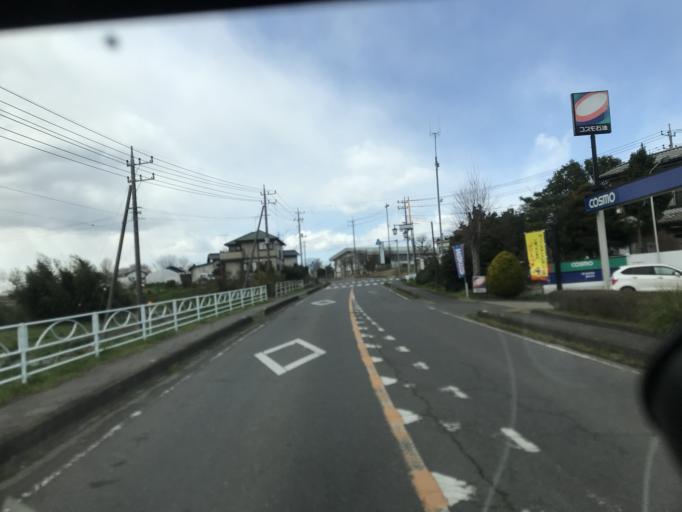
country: JP
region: Ibaraki
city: Shimodate
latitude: 36.2476
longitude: 139.9519
